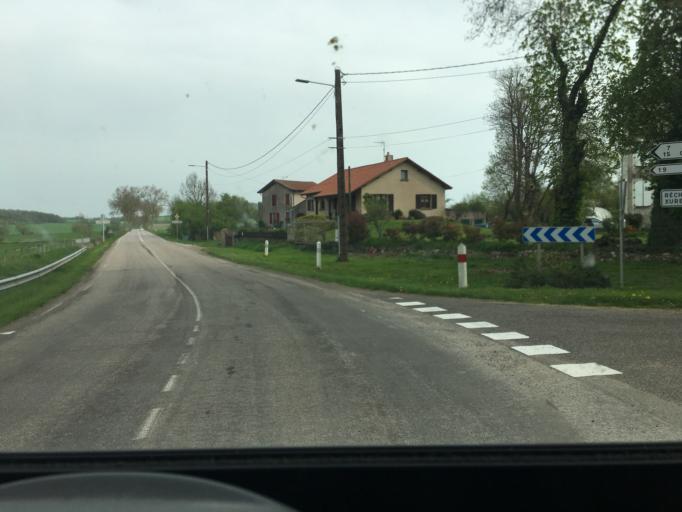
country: FR
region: Lorraine
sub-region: Departement de la Moselle
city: Vic-sur-Seille
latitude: 48.7255
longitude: 6.5380
